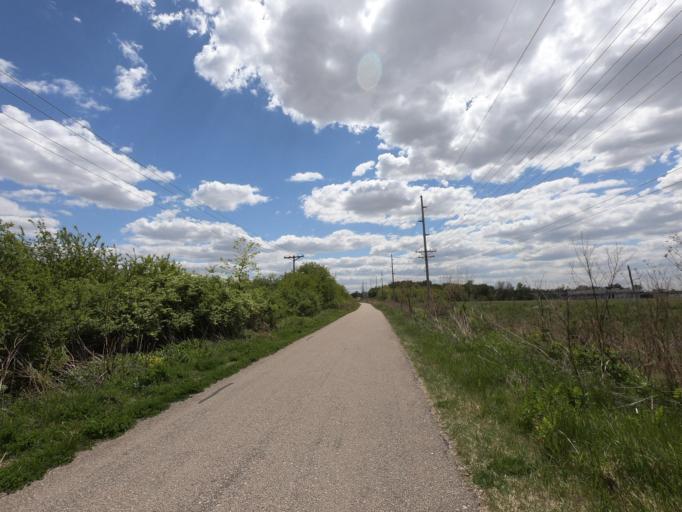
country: US
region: Wisconsin
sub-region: Dane County
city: Shorewood Hills
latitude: 43.0208
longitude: -89.4615
